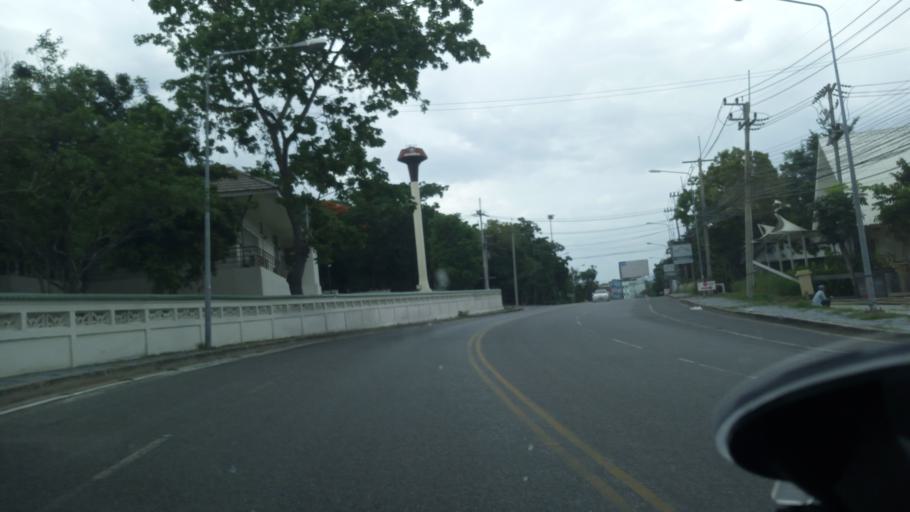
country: TH
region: Chon Buri
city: Chon Buri
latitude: 13.3064
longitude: 100.9056
